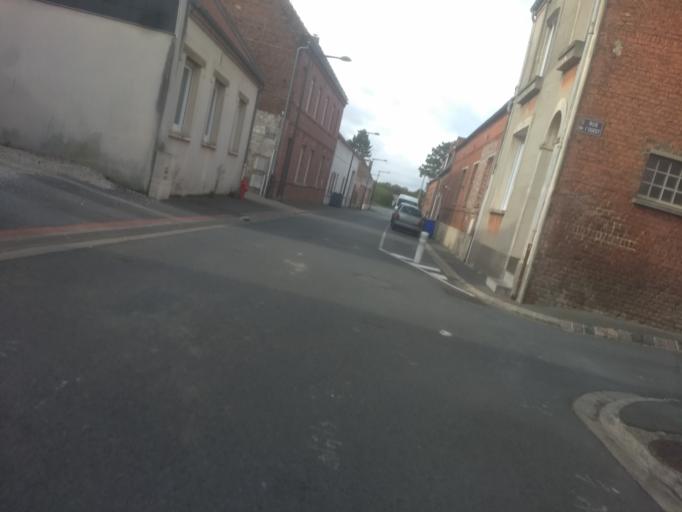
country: FR
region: Nord-Pas-de-Calais
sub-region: Departement du Pas-de-Calais
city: Dainville
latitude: 50.2807
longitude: 2.7192
